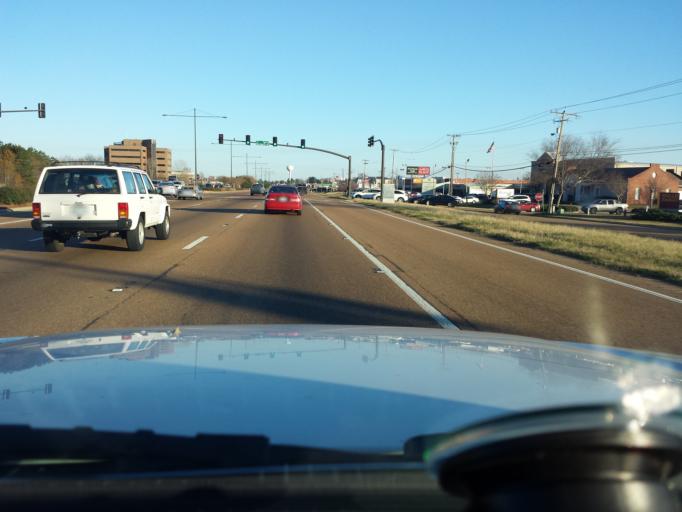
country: US
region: Mississippi
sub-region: Rankin County
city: Flowood
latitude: 32.3306
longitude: -90.1259
